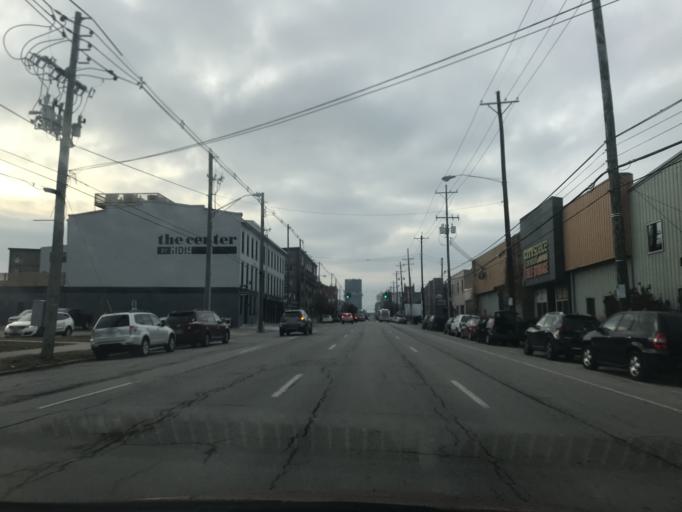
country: US
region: Indiana
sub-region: Clark County
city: Jeffersonville
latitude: 38.2543
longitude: -85.7347
